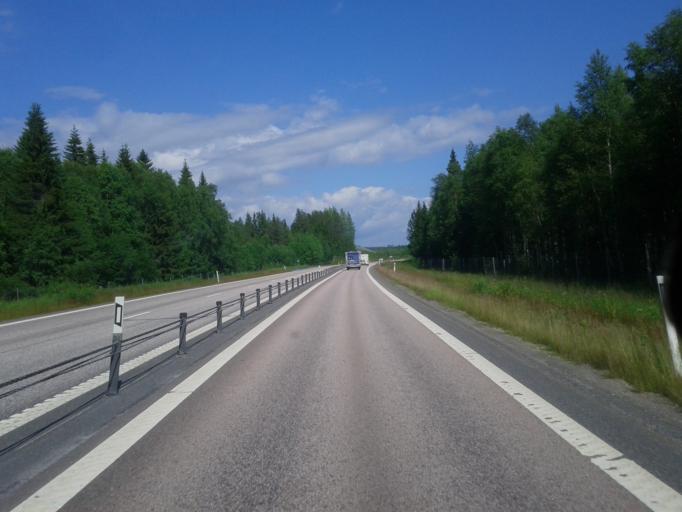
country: SE
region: Vaesternorrland
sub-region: OErnskoeldsviks Kommun
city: Husum
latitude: 63.4376
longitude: 19.2117
